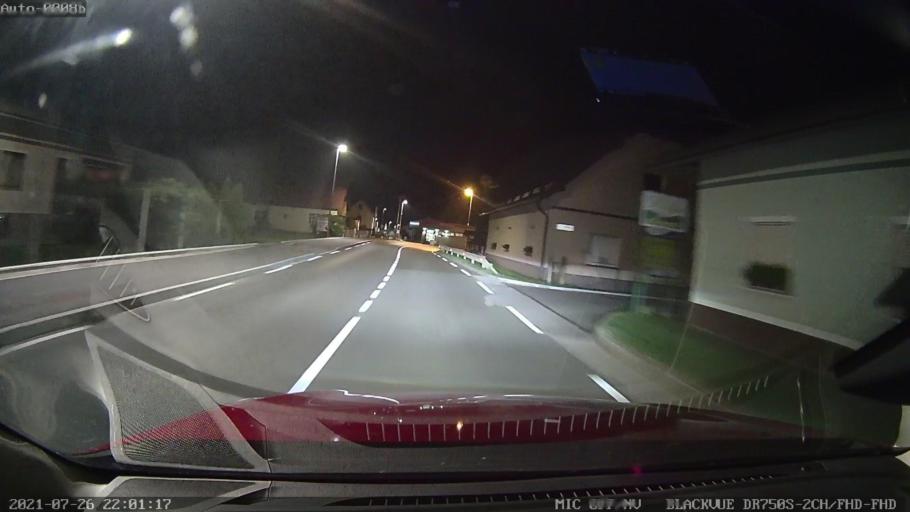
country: SI
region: Markovci
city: Markovci
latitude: 46.3880
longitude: 15.9575
